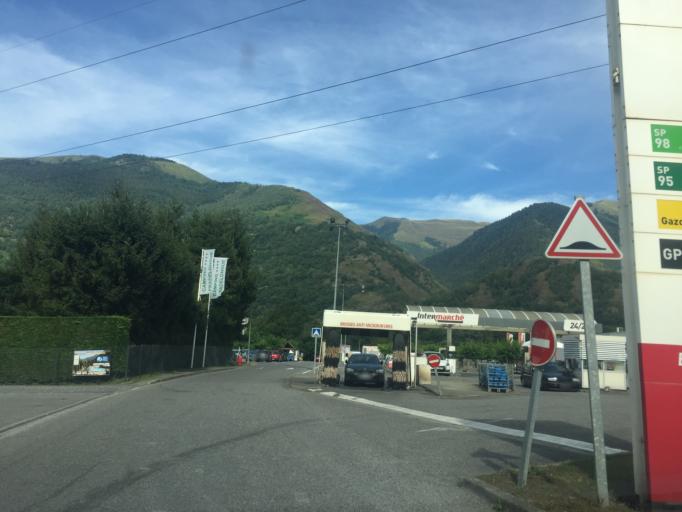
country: FR
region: Midi-Pyrenees
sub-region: Departement de la Haute-Garonne
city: Bagneres-de-Luchon
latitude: 42.8082
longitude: 0.5977
